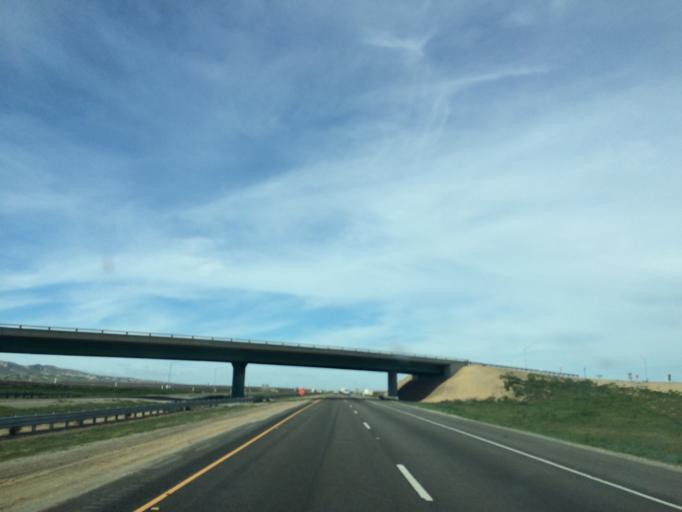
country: US
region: California
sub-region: Fresno County
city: Firebaugh
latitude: 36.6850
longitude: -120.6574
